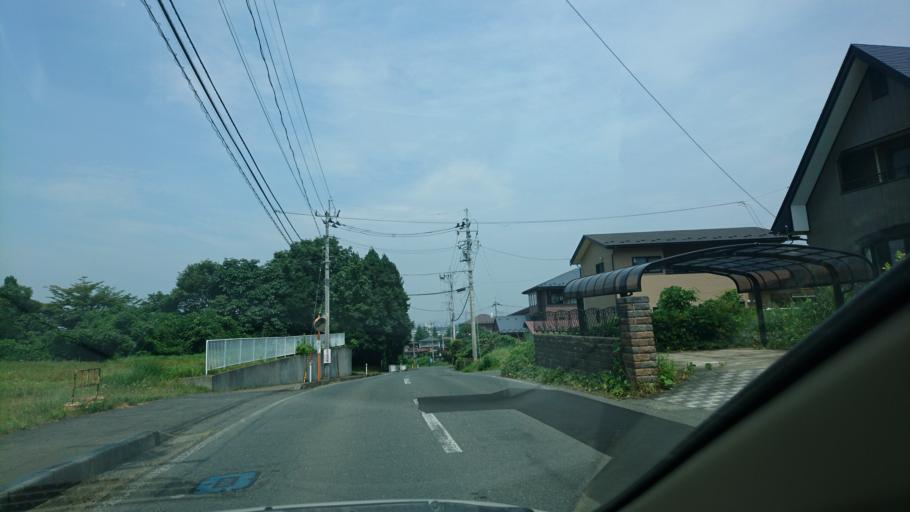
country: JP
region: Iwate
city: Kitakami
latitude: 39.2674
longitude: 141.0910
